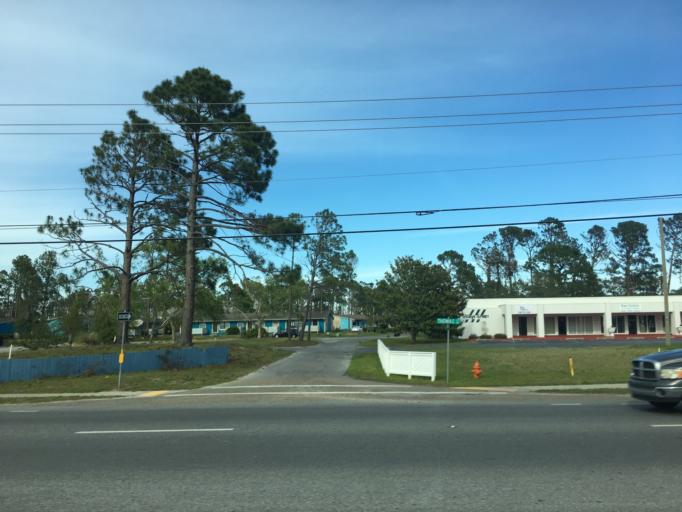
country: US
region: Florida
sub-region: Bay County
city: Upper Grand Lagoon
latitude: 30.1643
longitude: -85.7558
